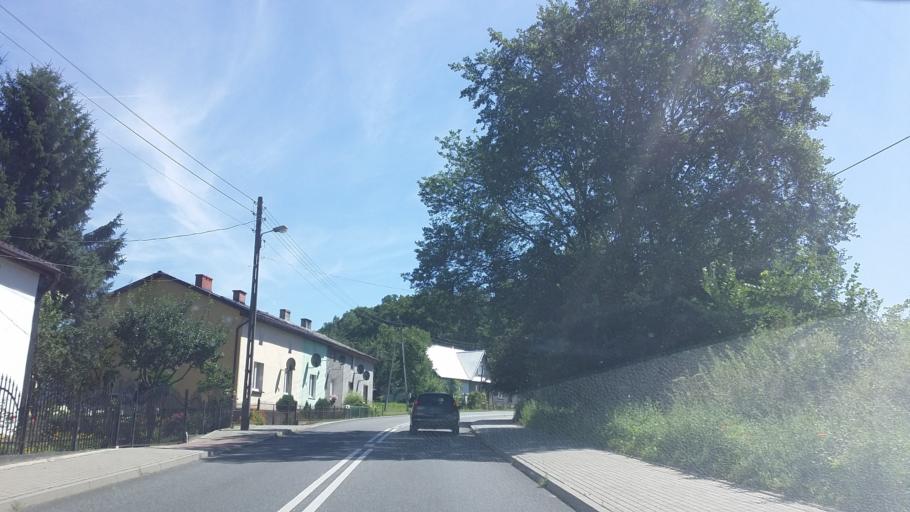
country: PL
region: West Pomeranian Voivodeship
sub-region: Powiat lobeski
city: Wegorzyno
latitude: 53.5146
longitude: 15.5734
